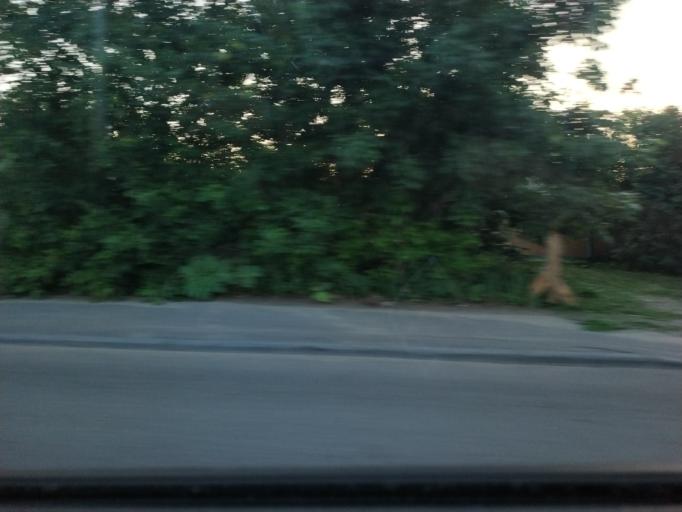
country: RU
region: Moskovskaya
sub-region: Shchelkovskiy Rayon
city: Grebnevo
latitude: 55.9788
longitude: 38.1154
